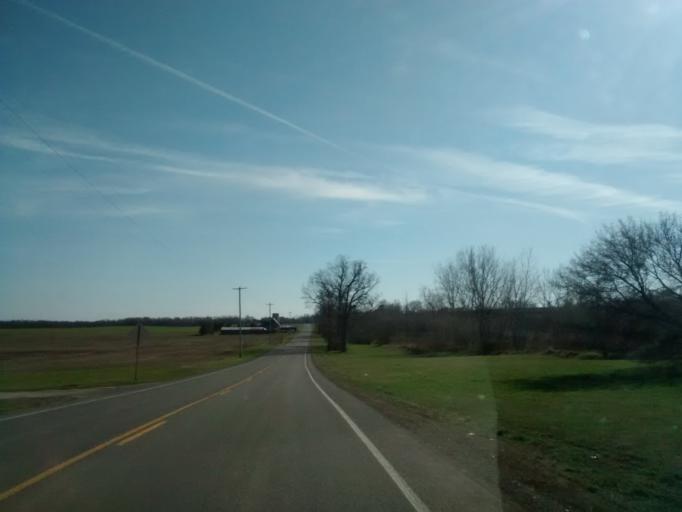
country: US
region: New York
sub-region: Monroe County
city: Scottsville
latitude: 42.9733
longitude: -77.7524
